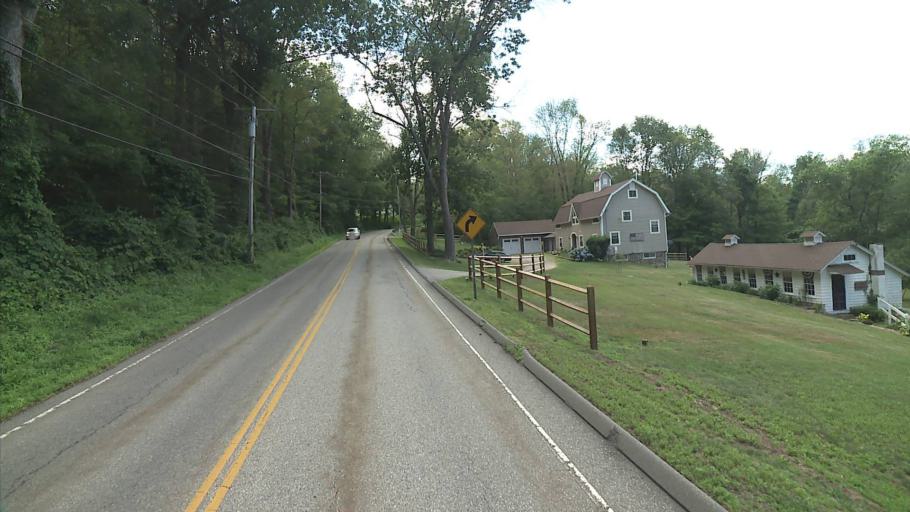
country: US
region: Connecticut
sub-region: Middlesex County
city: Higganum
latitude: 41.5438
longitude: -72.5450
